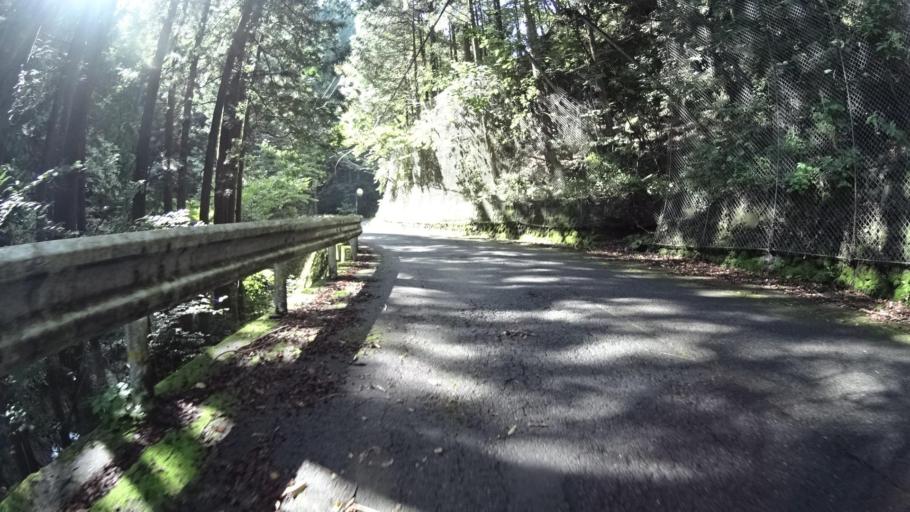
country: JP
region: Yamanashi
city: Uenohara
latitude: 35.7393
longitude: 139.0711
